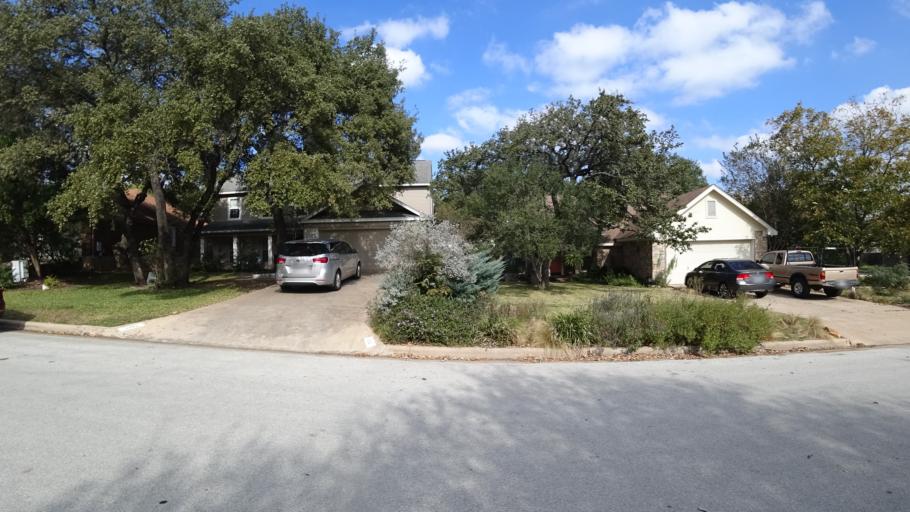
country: US
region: Texas
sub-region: Travis County
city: Shady Hollow
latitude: 30.1662
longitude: -97.8513
